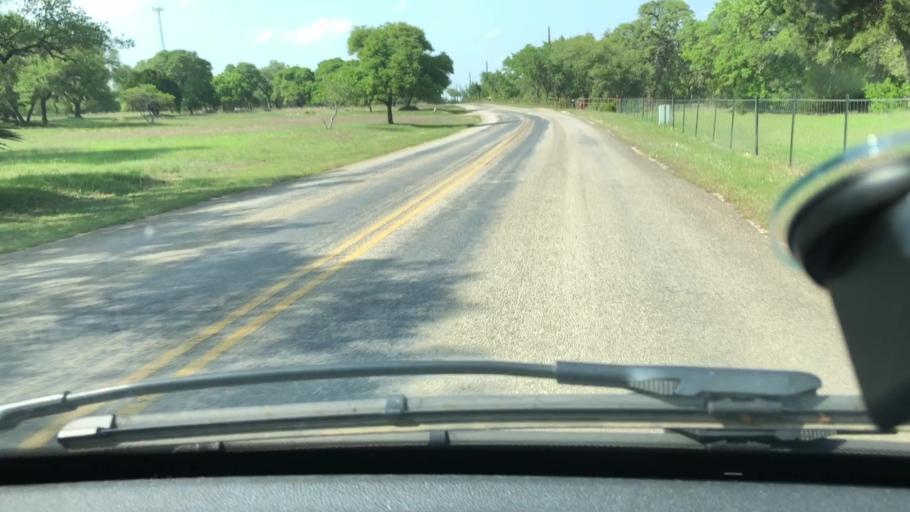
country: US
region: Texas
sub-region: Comal County
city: Bulverde
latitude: 29.7632
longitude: -98.4585
